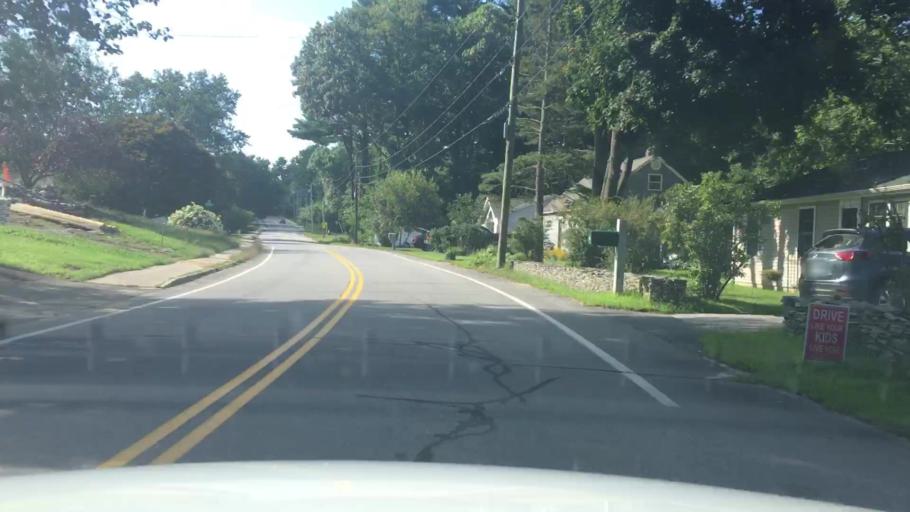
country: US
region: New Hampshire
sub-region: Strafford County
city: Dover
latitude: 43.1629
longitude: -70.8667
